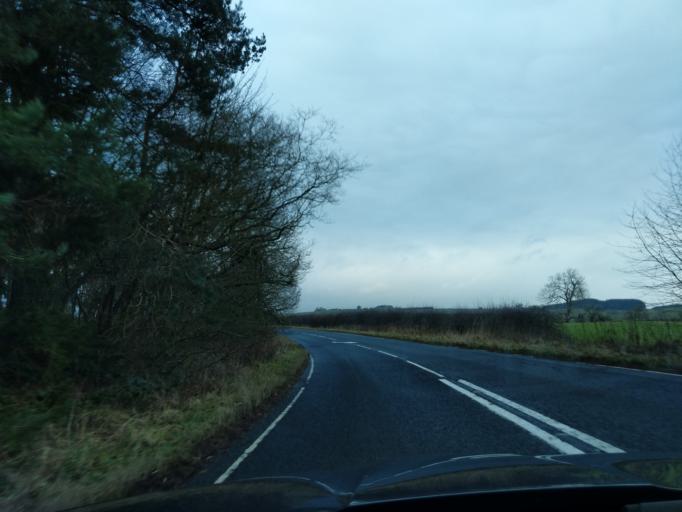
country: GB
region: England
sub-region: Northumberland
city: Rothley
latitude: 55.1462
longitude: -1.9930
